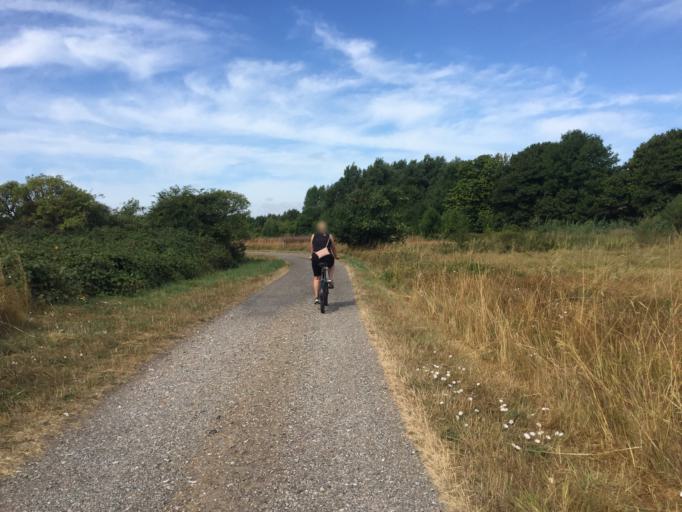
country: DK
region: Central Jutland
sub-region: Samso Kommune
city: Tranebjerg
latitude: 55.9571
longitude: 10.4146
